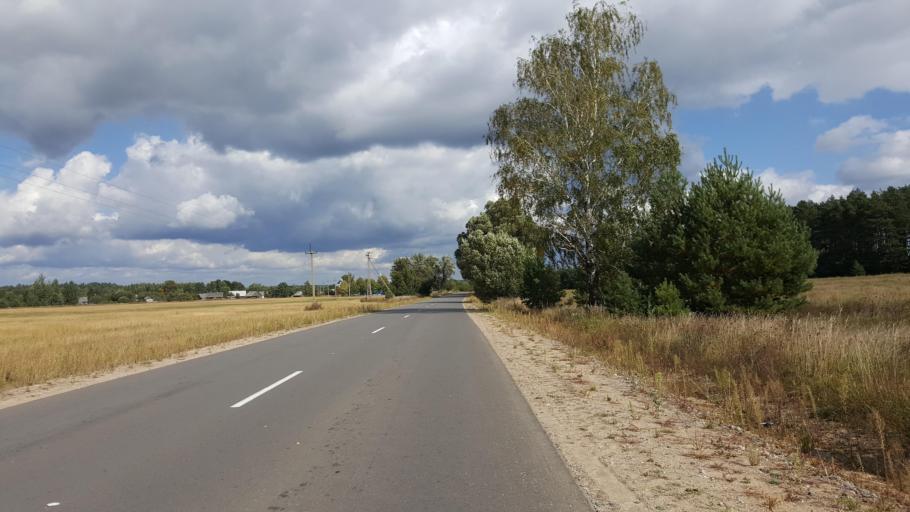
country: BY
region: Brest
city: Kamyanyets
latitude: 52.4131
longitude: 23.9192
